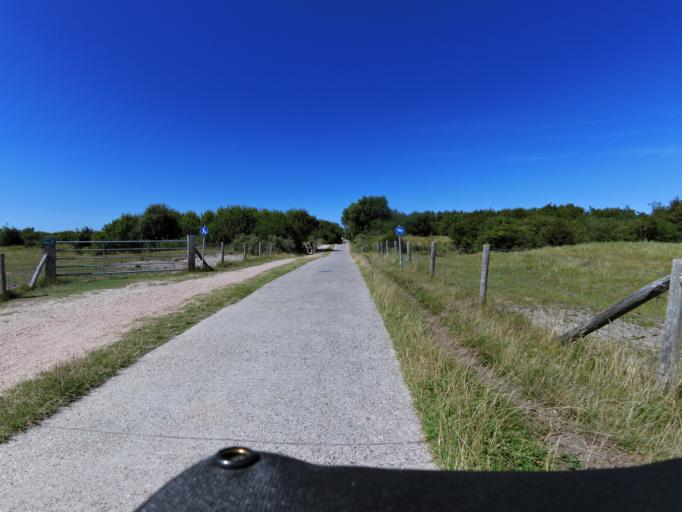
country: NL
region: Zeeland
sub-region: Schouwen-Duiveland
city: Haamstede
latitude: 51.7240
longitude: 3.7243
